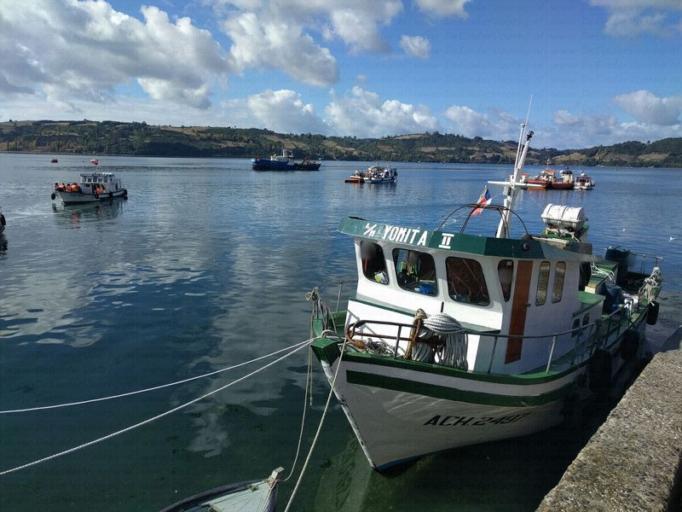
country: CL
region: Los Lagos
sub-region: Provincia de Chiloe
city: Castro
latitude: -42.4823
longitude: -73.7589
